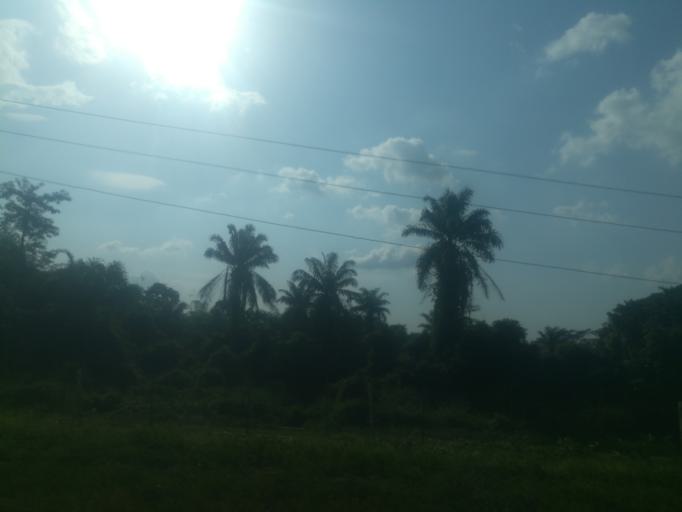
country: NG
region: Oyo
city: Moniya
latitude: 7.5058
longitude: 3.9129
